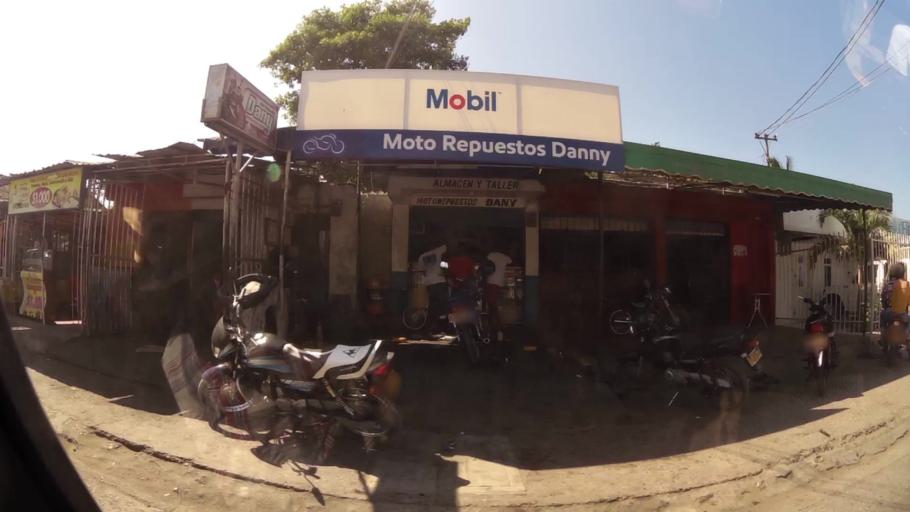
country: CO
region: Bolivar
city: Cartagena
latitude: 10.4162
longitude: -75.5198
